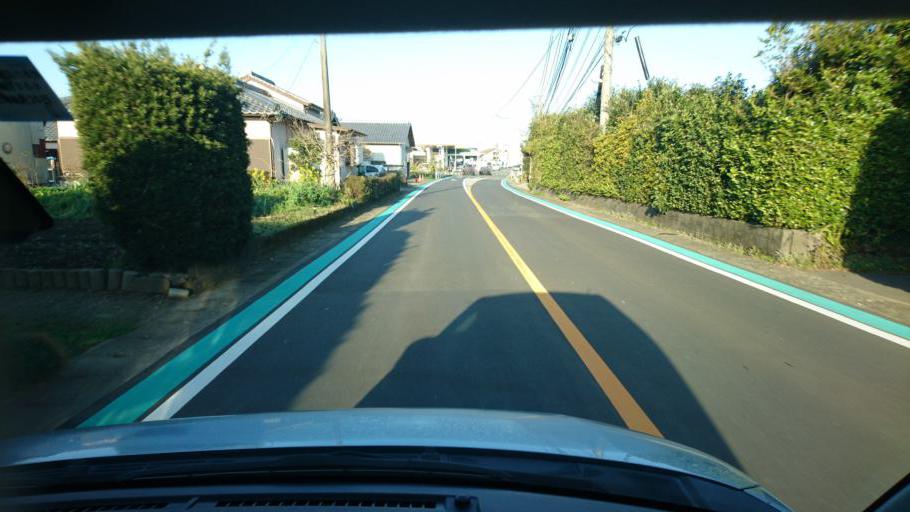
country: JP
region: Miyazaki
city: Miyazaki-shi
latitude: 31.8428
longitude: 131.4084
